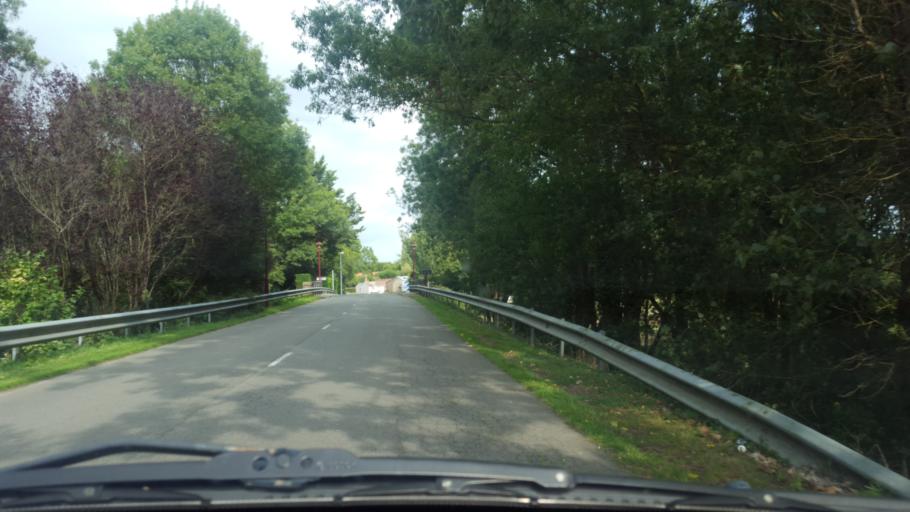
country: FR
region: Pays de la Loire
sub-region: Departement de la Loire-Atlantique
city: Saint-Meme-le-Tenu
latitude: 47.0212
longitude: -1.7926
